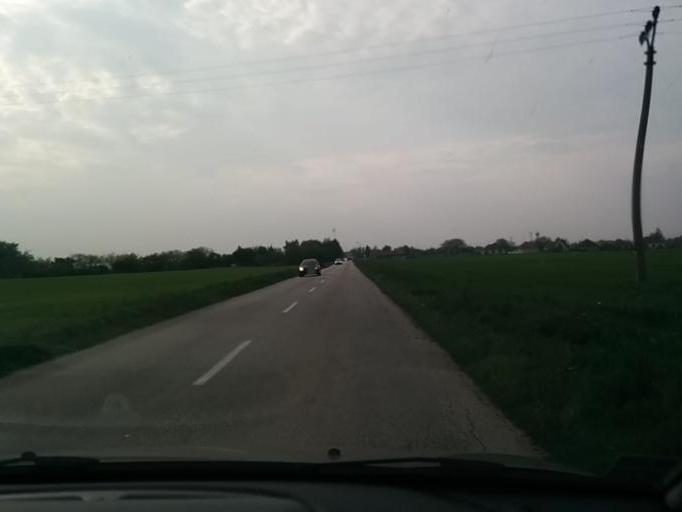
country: SK
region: Trnavsky
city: Sladkovicovo
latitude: 48.2241
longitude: 17.5827
